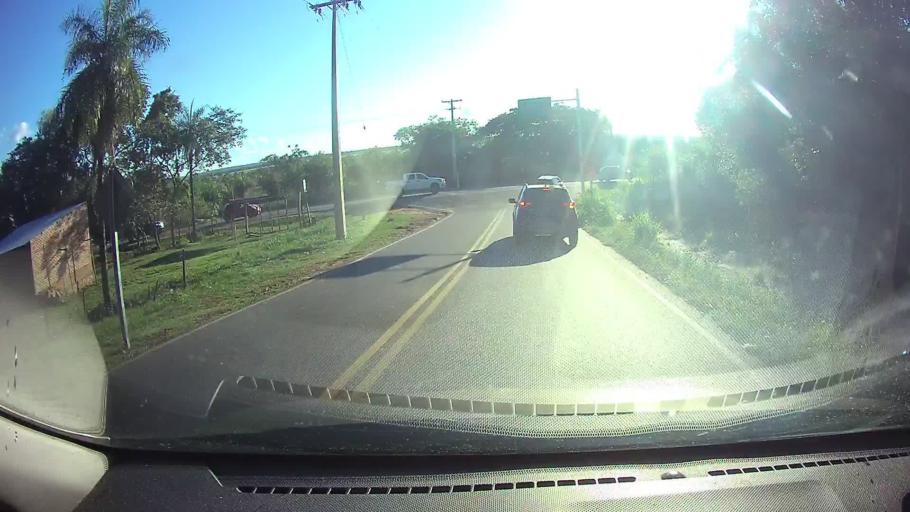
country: PY
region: Cordillera
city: Emboscada
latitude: -25.2078
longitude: -57.3526
